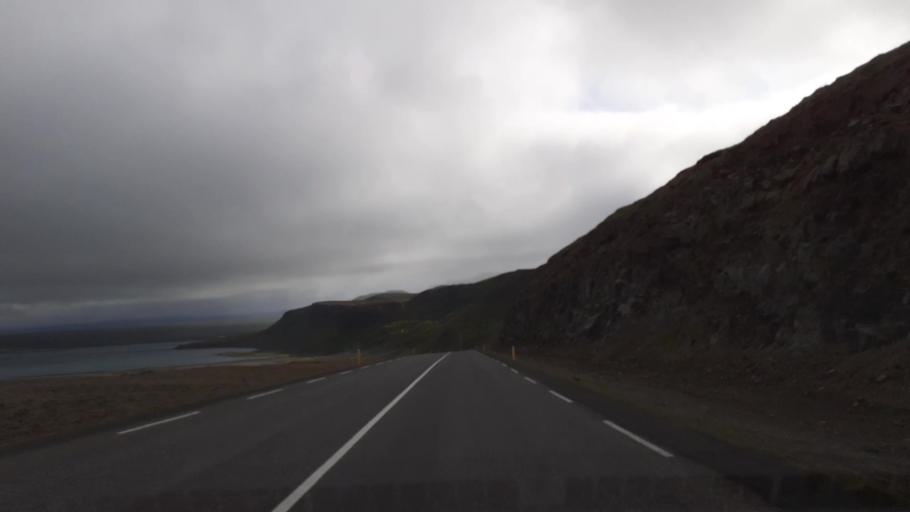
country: IS
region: Northeast
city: Husavik
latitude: 66.1328
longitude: -16.9513
